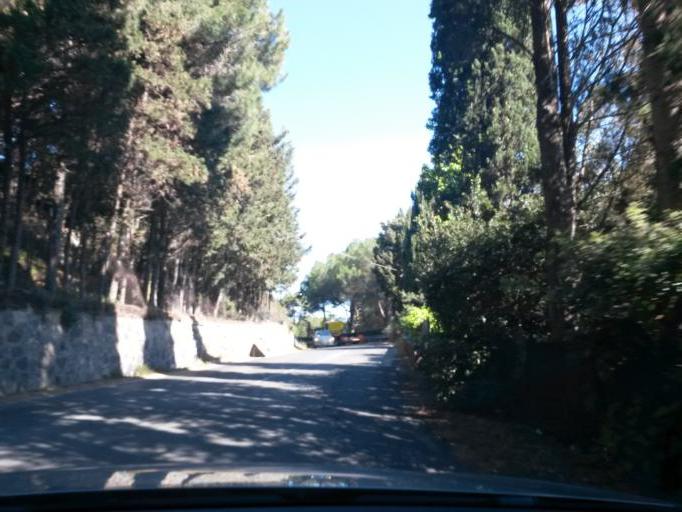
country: IT
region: Tuscany
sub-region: Provincia di Livorno
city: Marciana Marina
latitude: 42.7927
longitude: 10.2193
